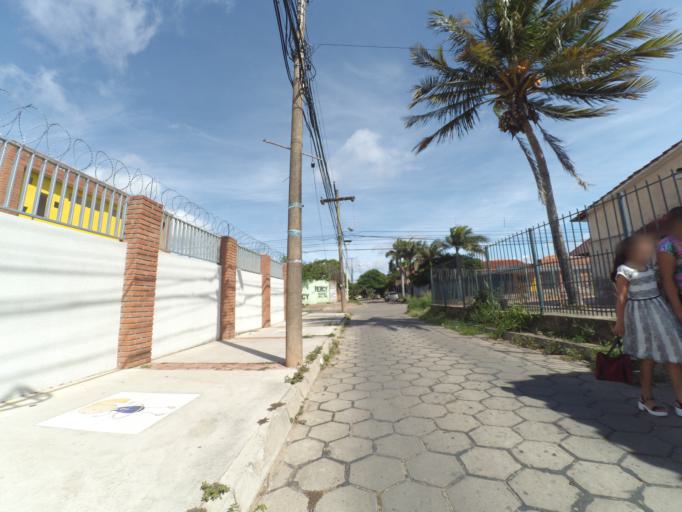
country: BO
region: Santa Cruz
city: Santa Cruz de la Sierra
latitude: -17.7614
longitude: -63.1555
